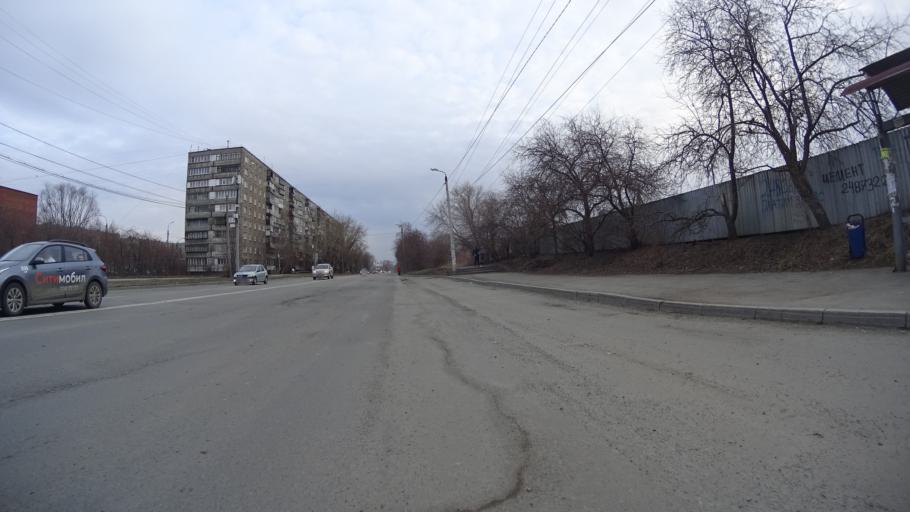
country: RU
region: Chelyabinsk
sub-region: Gorod Chelyabinsk
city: Chelyabinsk
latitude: 55.1908
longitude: 61.4826
